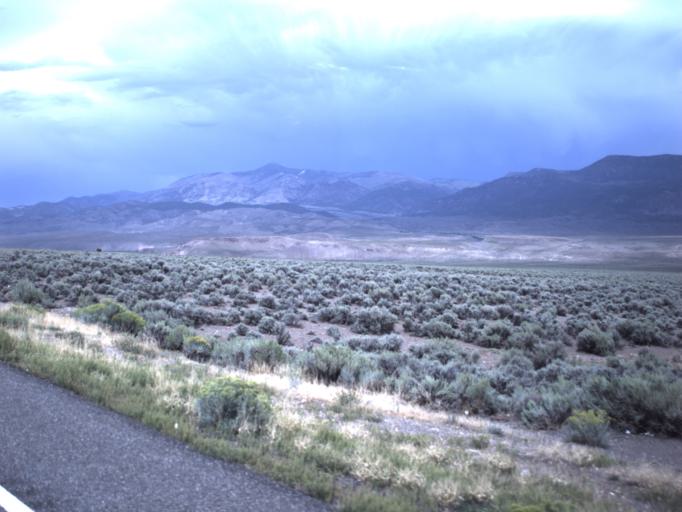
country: US
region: Utah
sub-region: Piute County
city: Junction
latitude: 38.3373
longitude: -112.2176
